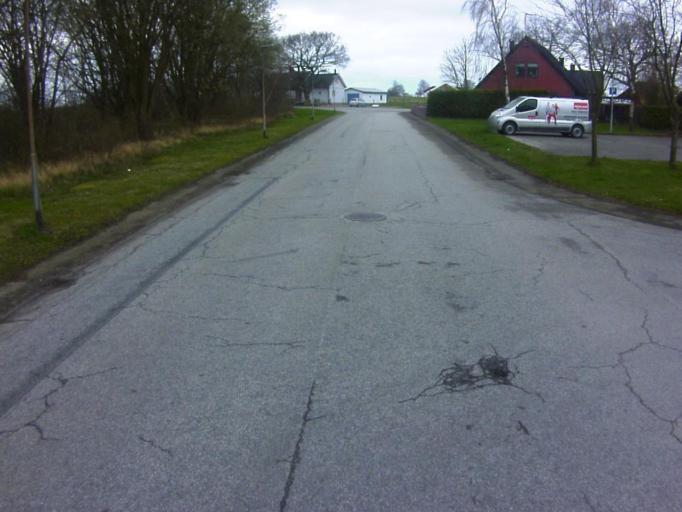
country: SE
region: Skane
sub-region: Kavlinge Kommun
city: Kaevlinge
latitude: 55.7685
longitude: 13.0858
